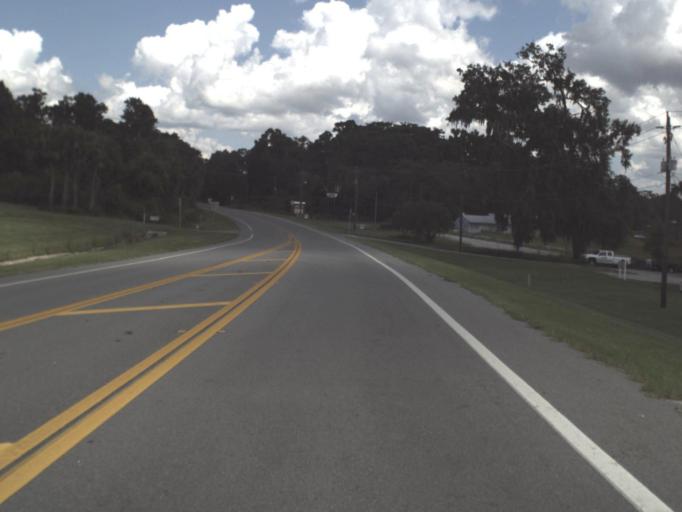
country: US
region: Florida
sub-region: Putnam County
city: Crescent City
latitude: 29.4489
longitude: -81.5117
